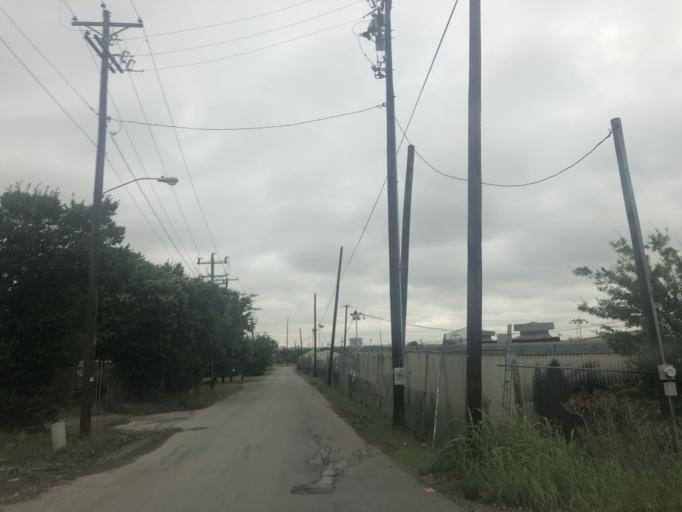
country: US
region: Texas
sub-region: Dallas County
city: Cockrell Hill
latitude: 32.7762
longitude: -96.8652
